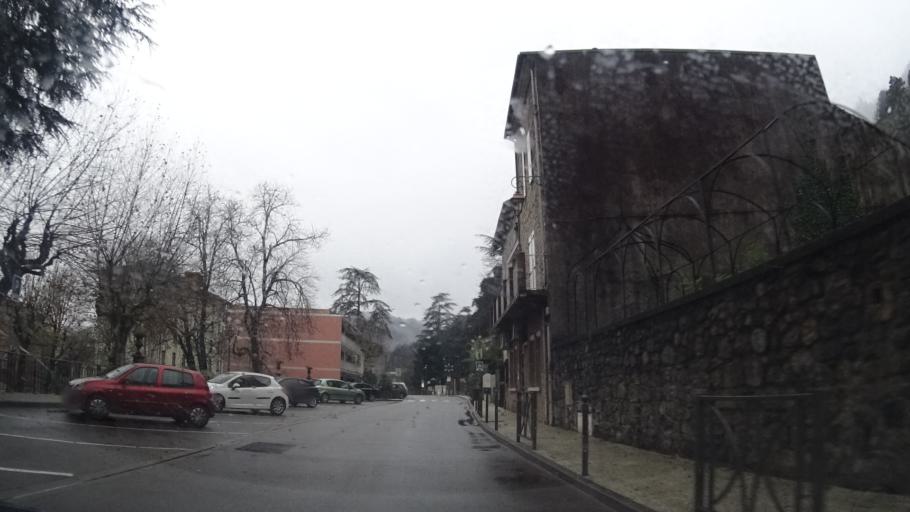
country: FR
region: Rhone-Alpes
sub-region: Departement de l'Ardeche
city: Vals-les-Bains
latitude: 44.6571
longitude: 4.3659
